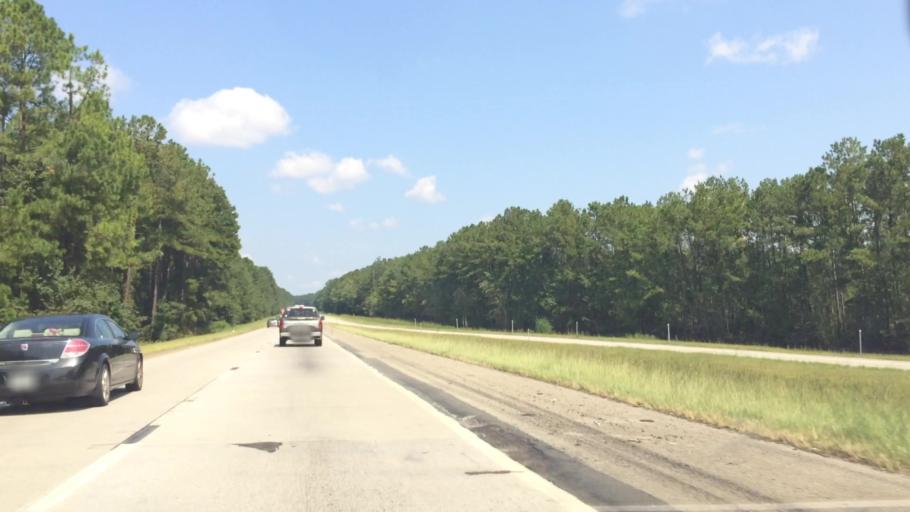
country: US
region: South Carolina
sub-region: Colleton County
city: Walterboro
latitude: 33.0050
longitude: -80.6685
